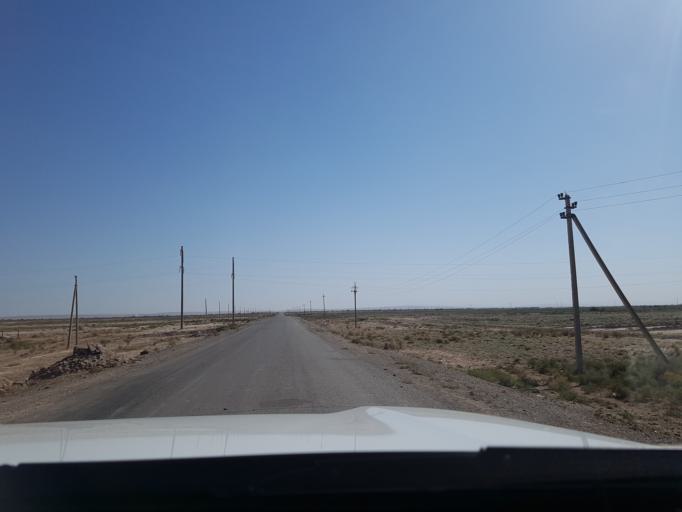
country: IR
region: Razavi Khorasan
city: Sarakhs
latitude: 36.5107
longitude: 61.2532
